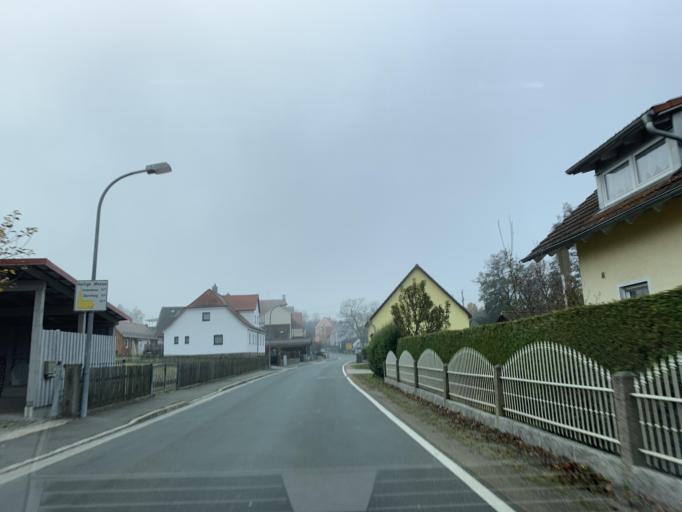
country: DE
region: Bavaria
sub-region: Upper Palatinate
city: Neunburg vorm Wald
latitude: 49.3511
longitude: 12.3898
